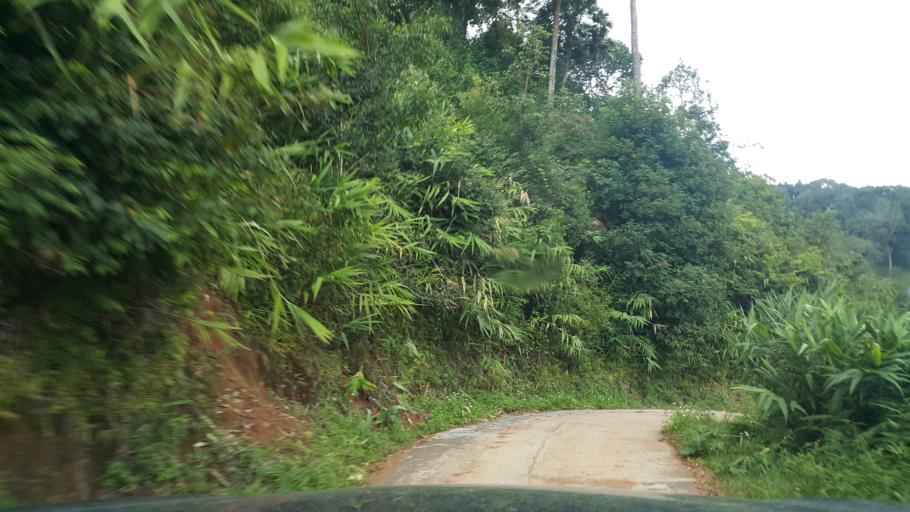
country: TH
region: Lampang
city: Wang Nuea
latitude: 19.1133
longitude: 99.3655
